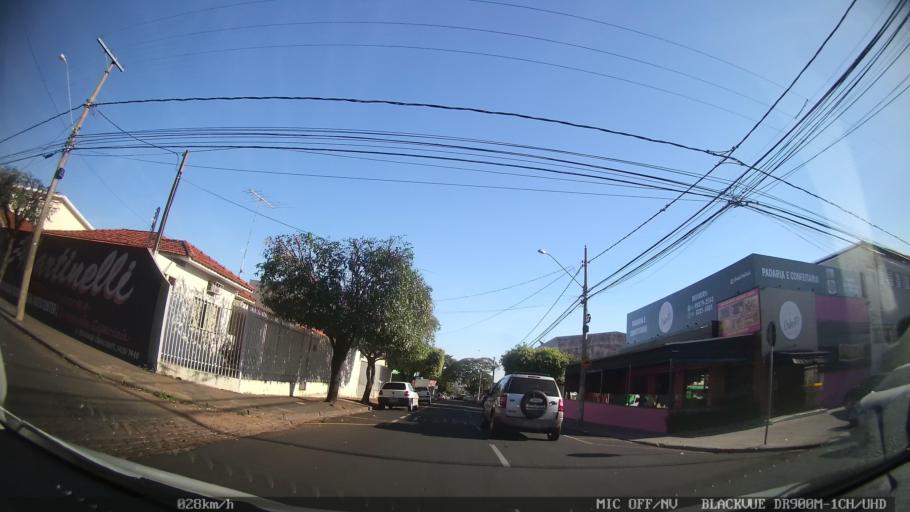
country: BR
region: Sao Paulo
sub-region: Sao Jose Do Rio Preto
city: Sao Jose do Rio Preto
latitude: -20.7956
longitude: -49.3654
